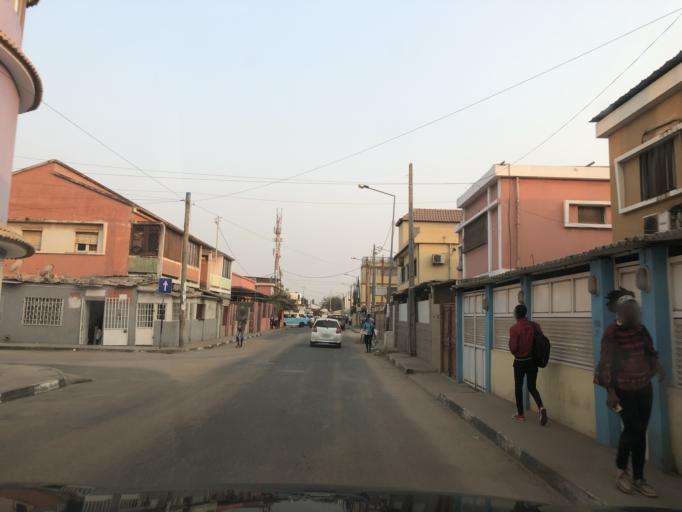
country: AO
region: Luanda
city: Luanda
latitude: -8.8465
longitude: 13.2270
